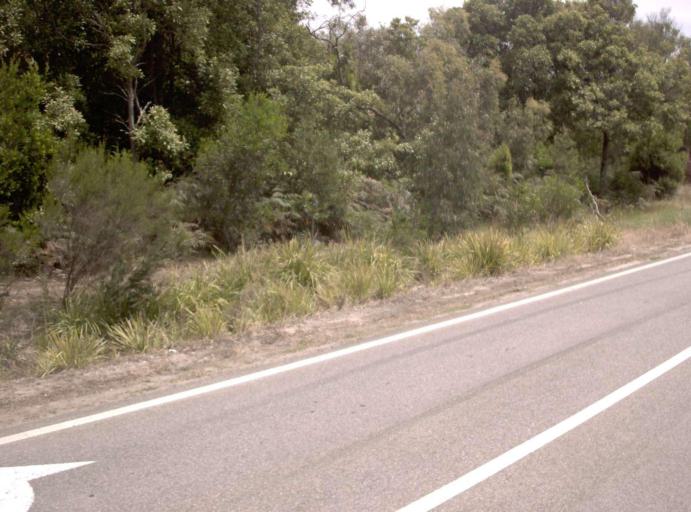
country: AU
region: Victoria
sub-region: Casey
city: Cranbourne South
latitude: -38.1460
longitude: 145.2259
